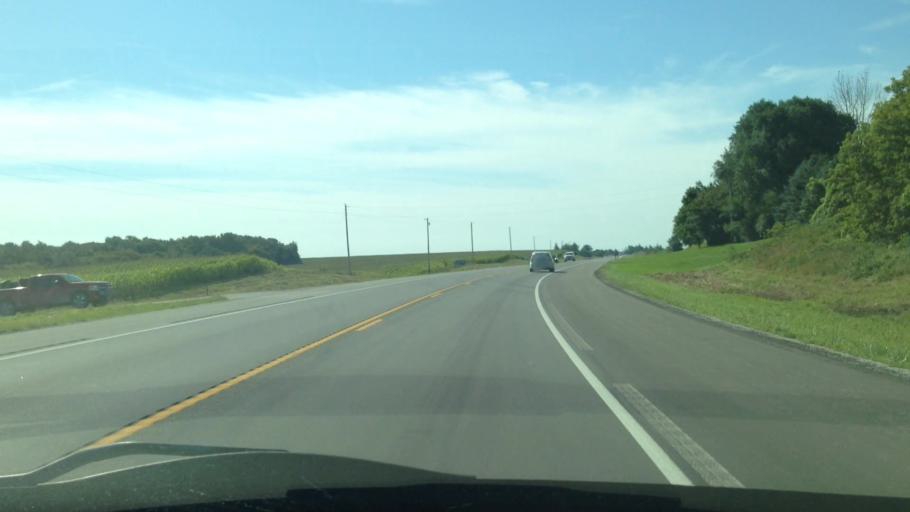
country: US
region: Minnesota
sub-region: Fillmore County
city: Harmony
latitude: 43.6076
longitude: -92.0100
